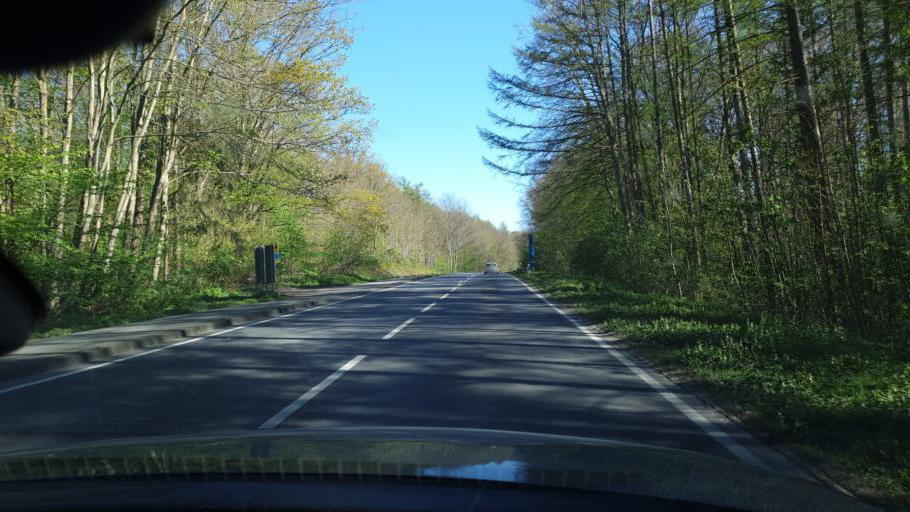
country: DE
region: Mecklenburg-Vorpommern
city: Werdervorstadt
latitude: 53.6508
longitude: 11.4317
